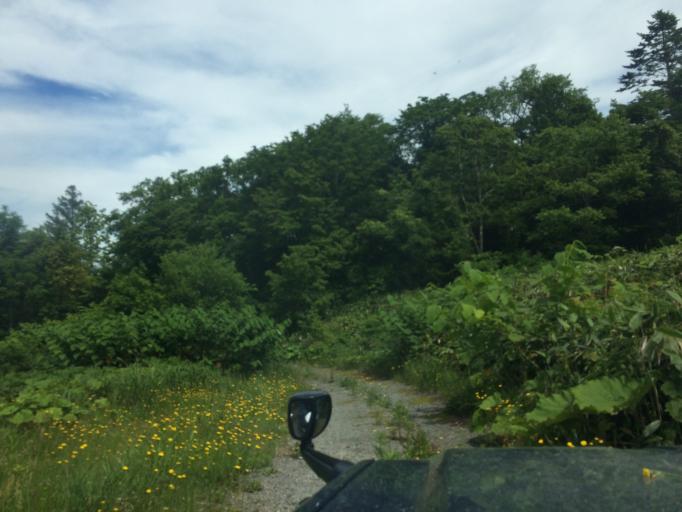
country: JP
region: Hokkaido
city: Niseko Town
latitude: 42.8603
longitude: 140.7949
